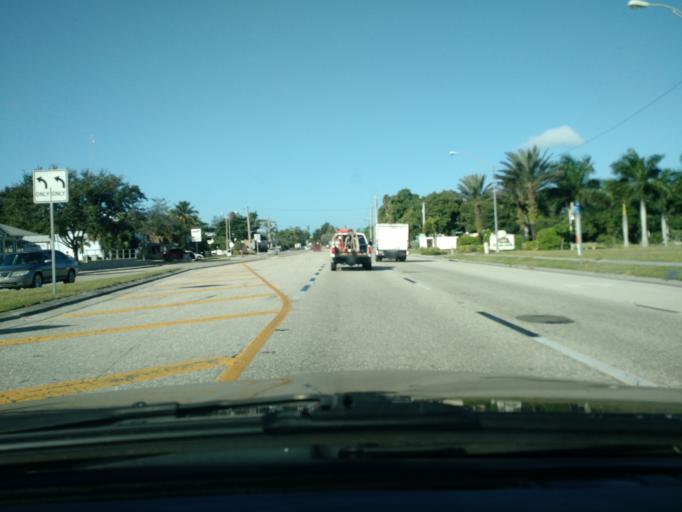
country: US
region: Florida
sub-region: Lee County
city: Bonita Springs
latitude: 26.3306
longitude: -81.8172
